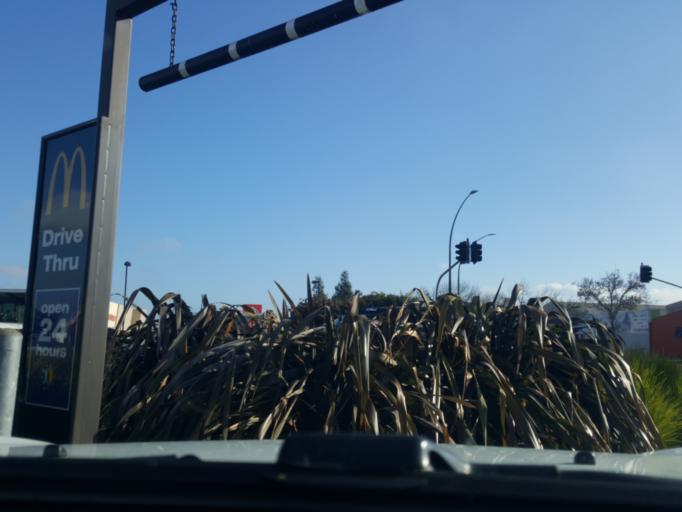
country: NZ
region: Waikato
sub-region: Hamilton City
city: Hamilton
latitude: -37.7521
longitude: 175.2407
